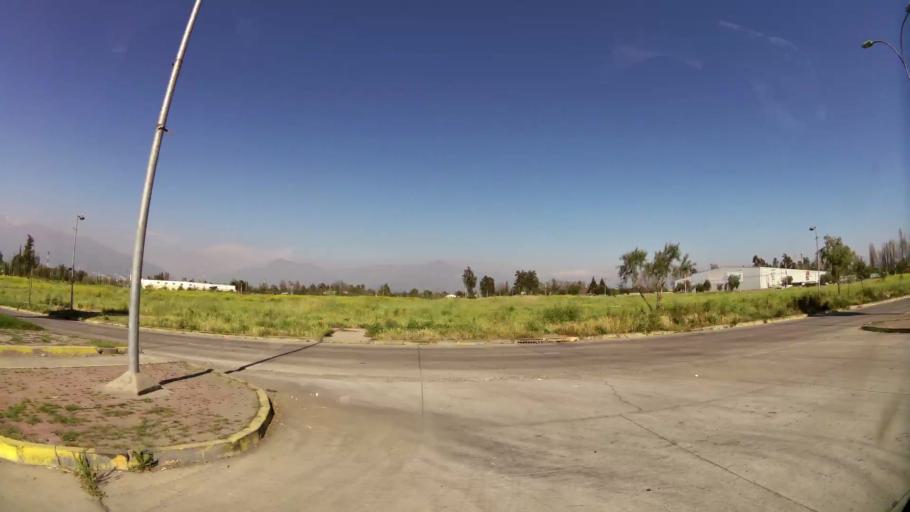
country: CL
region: Santiago Metropolitan
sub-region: Provincia de Santiago
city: La Pintana
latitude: -33.5869
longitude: -70.6339
